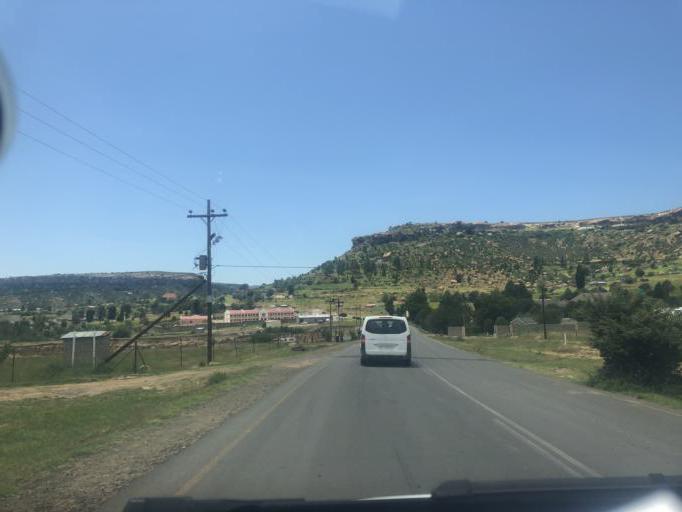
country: LS
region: Maseru
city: Maseru
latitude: -29.3508
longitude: 27.6575
